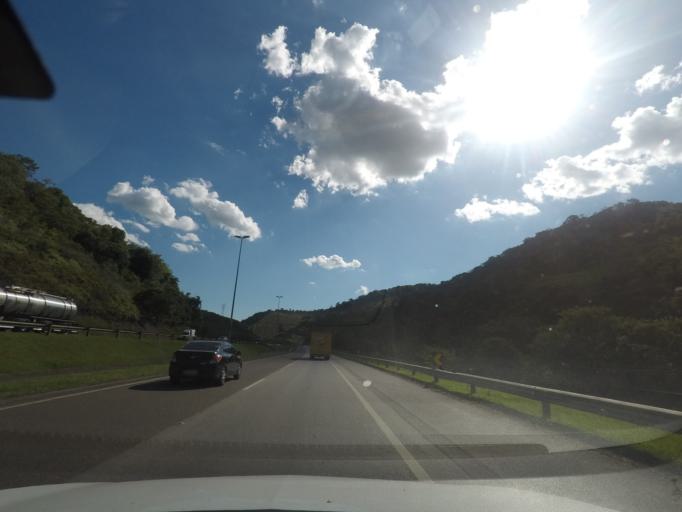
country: BR
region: Rio de Janeiro
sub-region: Guapimirim
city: Guapimirim
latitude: -22.5704
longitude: -43.0058
